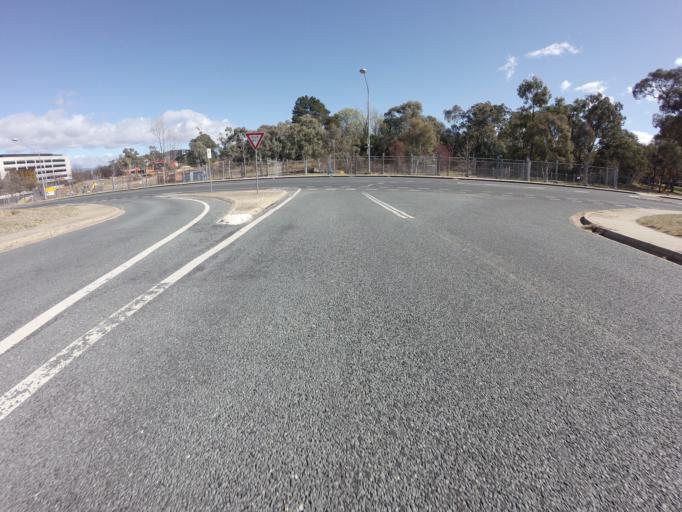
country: AU
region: Australian Capital Territory
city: Canberra
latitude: -35.2922
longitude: 149.1478
